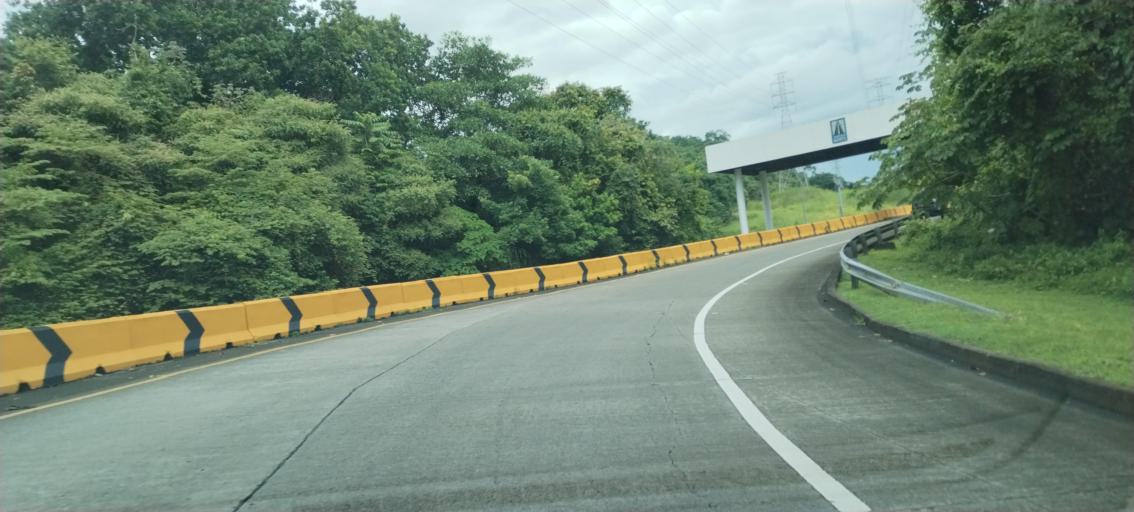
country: PA
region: Panama
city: Panama
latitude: 8.9915
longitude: -79.5408
